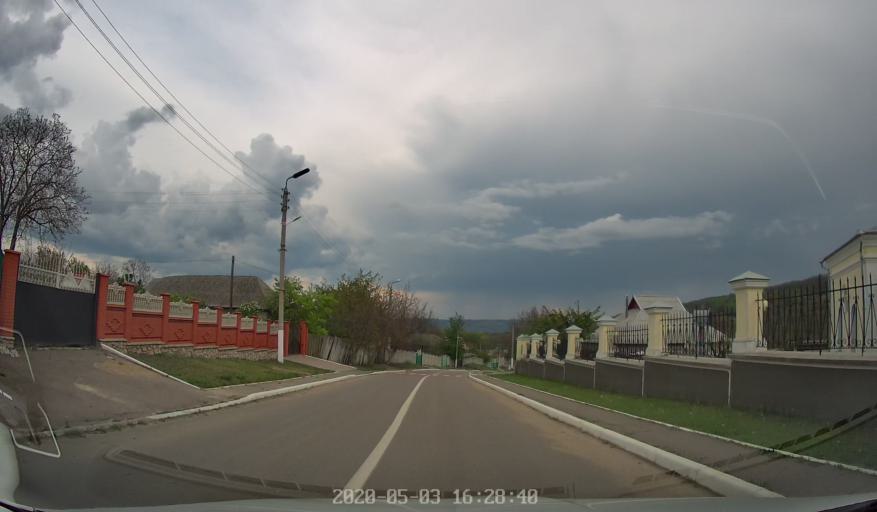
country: MD
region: Calarasi
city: Calarasi
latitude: 47.1922
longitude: 28.3530
